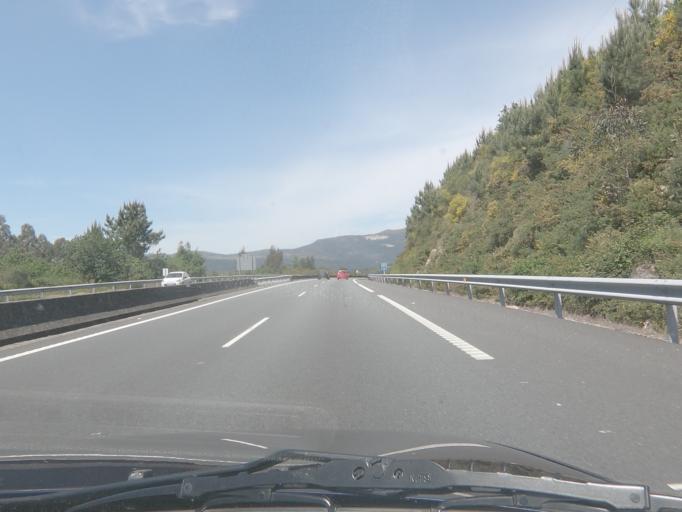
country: ES
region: Galicia
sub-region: Provincia de Pontevedra
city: Portas
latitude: 42.5719
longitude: -8.6717
